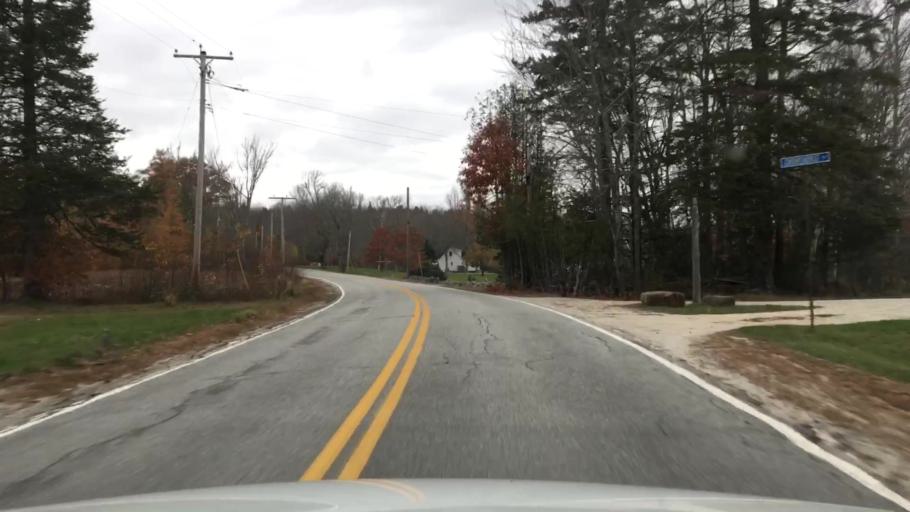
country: US
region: Maine
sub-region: Hancock County
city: Sedgwick
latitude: 44.3007
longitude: -68.5601
